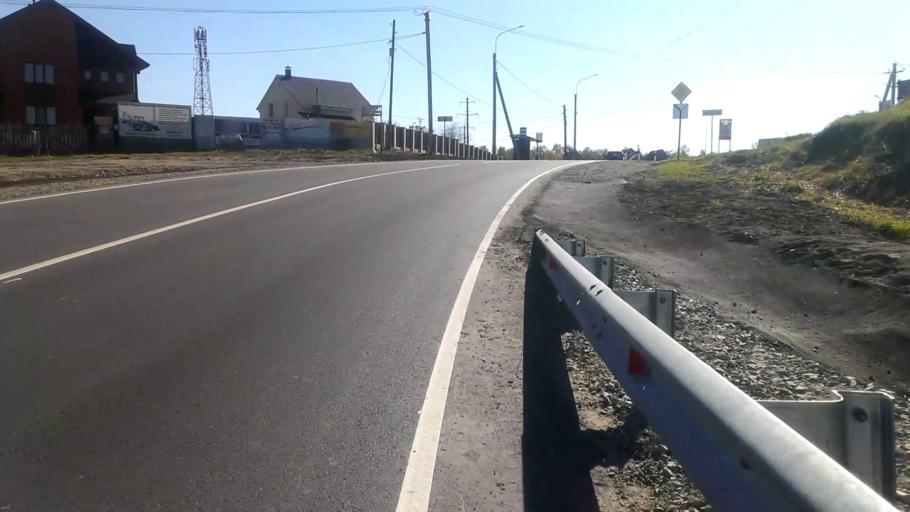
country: RU
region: Altai Krai
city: Sannikovo
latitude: 53.3193
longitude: 83.9444
